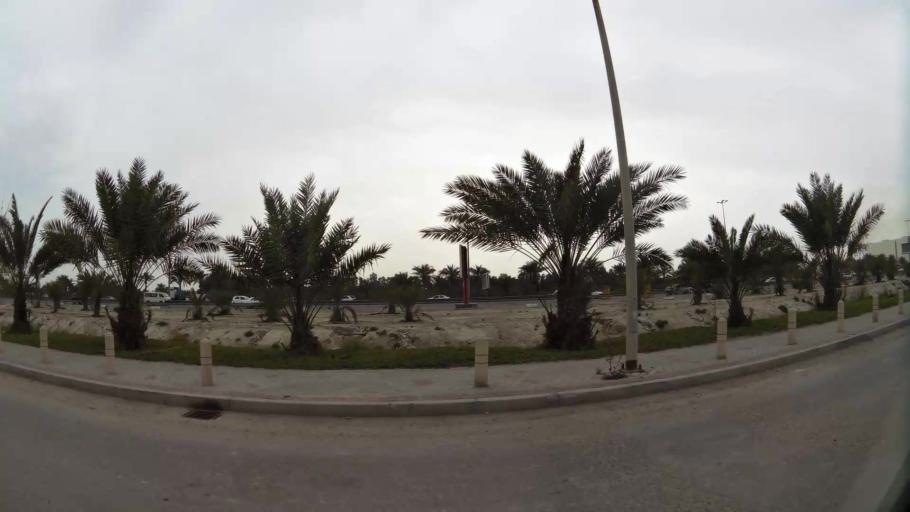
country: BH
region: Manama
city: Jidd Hafs
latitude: 26.1979
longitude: 50.5485
